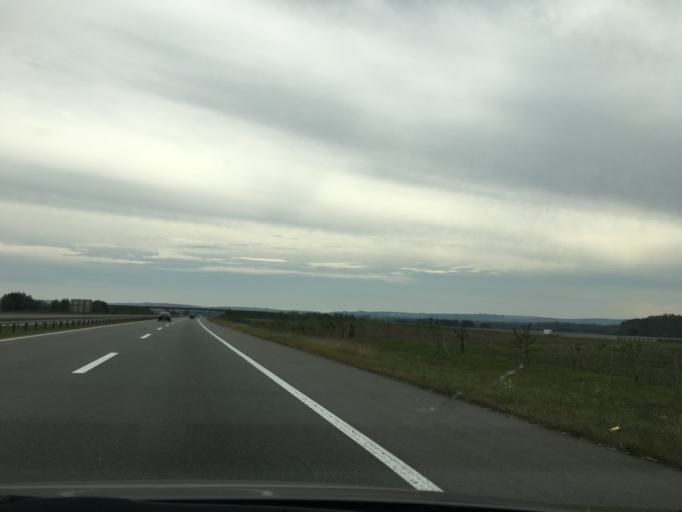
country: RS
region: Autonomna Pokrajina Vojvodina
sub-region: Juznobacki Okrug
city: Kovilj
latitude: 45.2120
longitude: 20.0667
